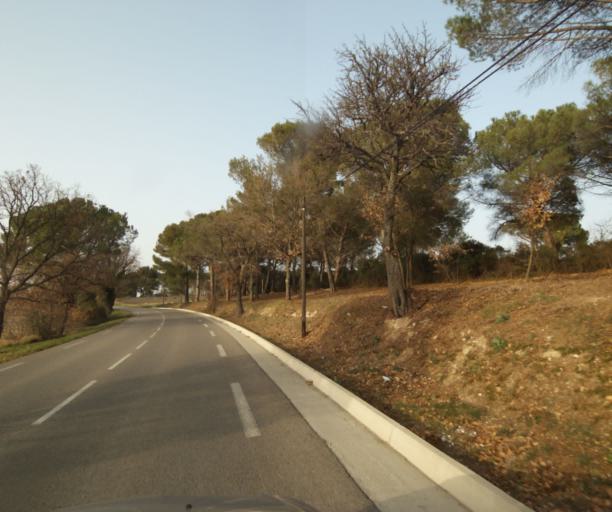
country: FR
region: Provence-Alpes-Cote d'Azur
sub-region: Departement des Bouches-du-Rhone
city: Eguilles
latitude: 43.5911
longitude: 5.3674
